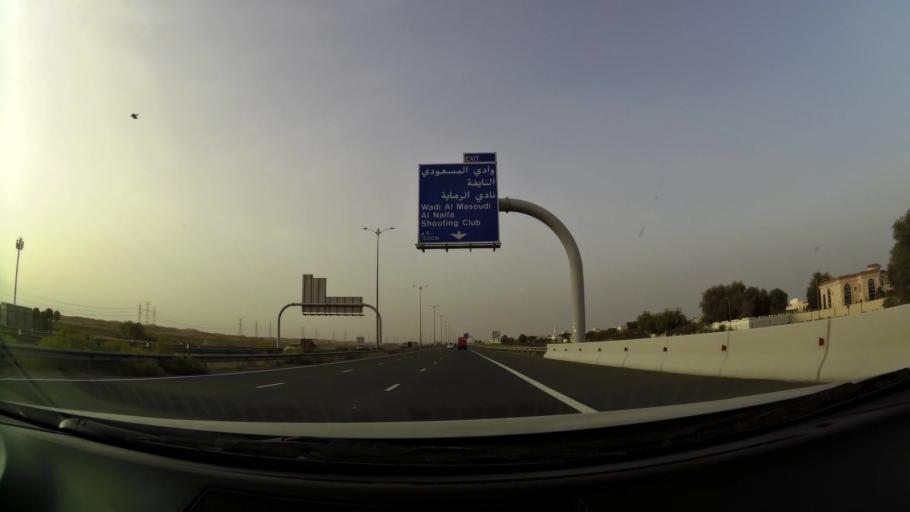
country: OM
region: Al Buraimi
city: Al Buraymi
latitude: 24.2848
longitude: 55.7335
